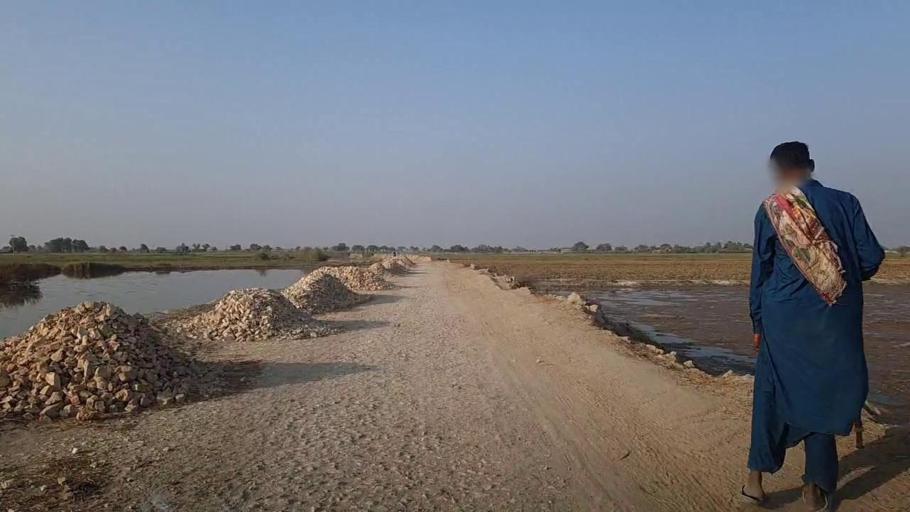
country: PK
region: Sindh
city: Tangwani
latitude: 28.2480
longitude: 69.0690
